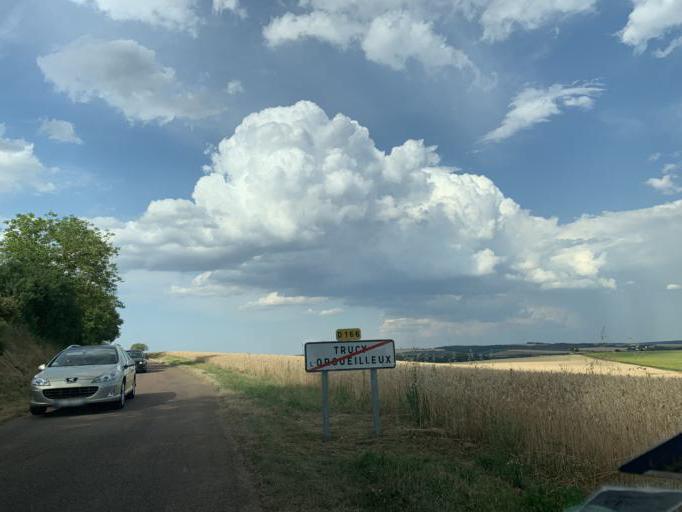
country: FR
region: Bourgogne
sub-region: Departement de la Nievre
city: Clamecy
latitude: 47.4509
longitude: 3.4188
